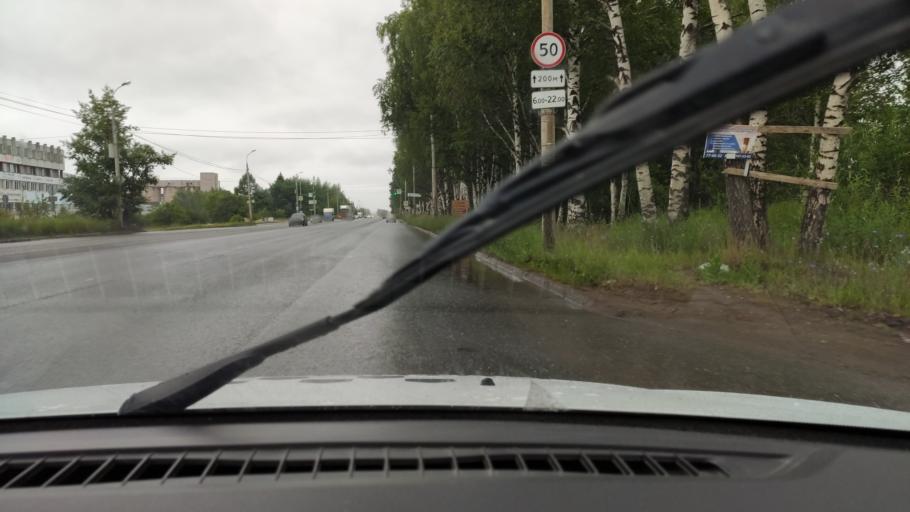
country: RU
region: Udmurtiya
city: Khokhryaki
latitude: 56.9069
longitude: 53.3496
